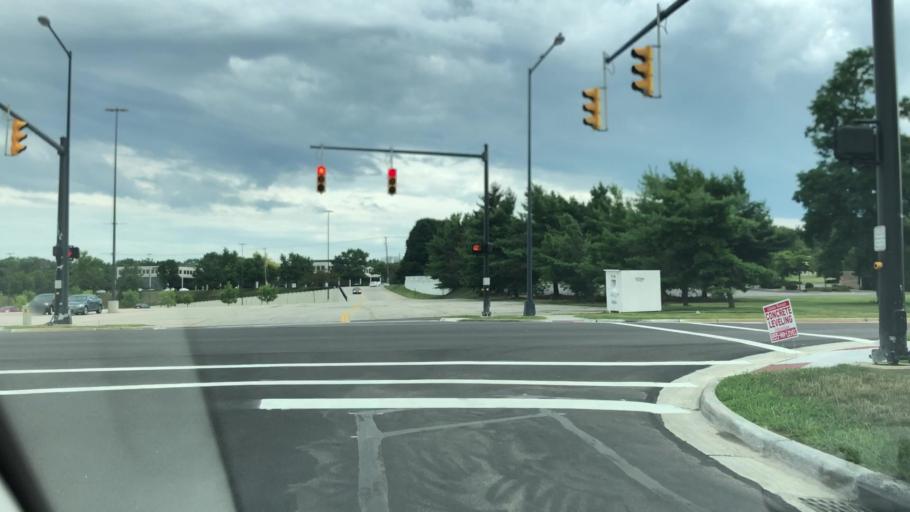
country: US
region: Ohio
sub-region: Summit County
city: Fairlawn
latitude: 41.1361
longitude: -81.6213
